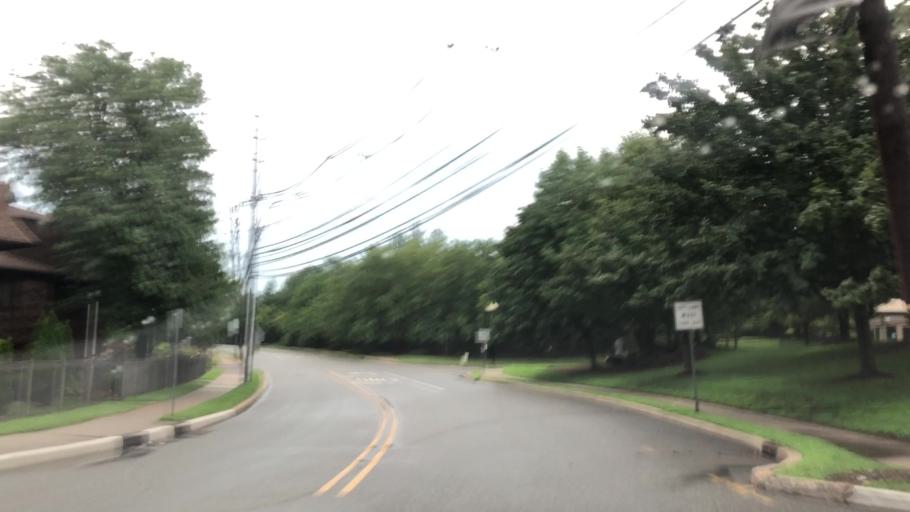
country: US
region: New Jersey
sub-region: Bergen County
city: Lyndhurst
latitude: 40.8257
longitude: -74.1337
